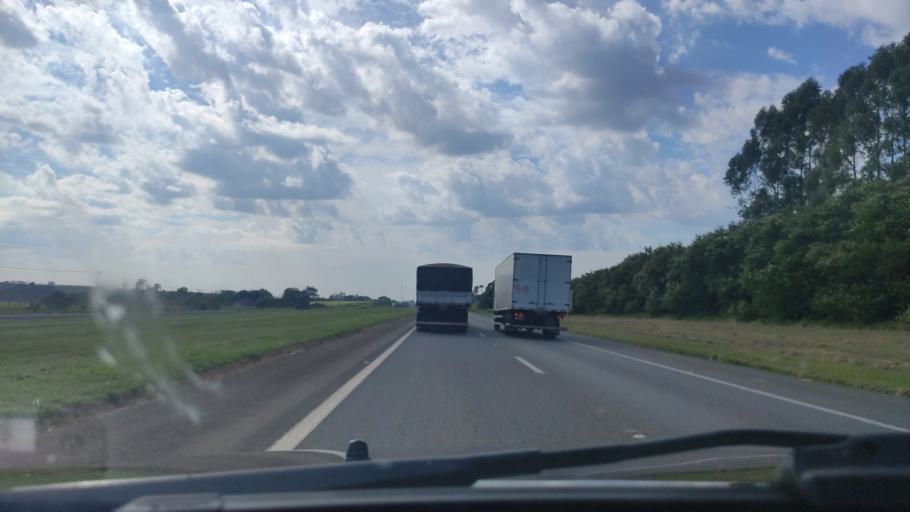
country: BR
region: Sao Paulo
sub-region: Porangaba
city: Porangaba
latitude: -23.2507
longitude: -47.9812
